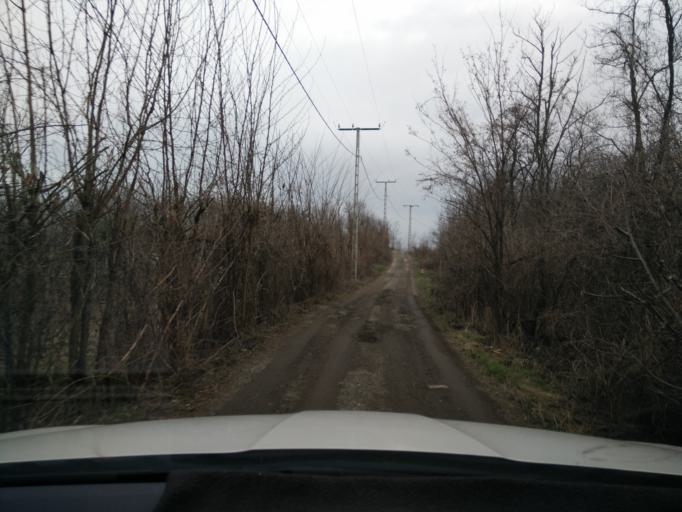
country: HU
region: Tolna
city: Szekszard
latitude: 46.3482
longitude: 18.6686
